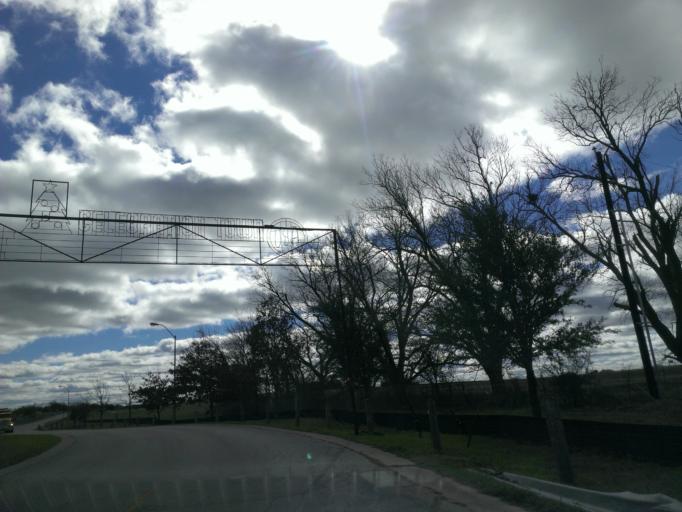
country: US
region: Texas
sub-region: Williamson County
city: Round Rock
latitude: 30.5432
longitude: -97.6295
